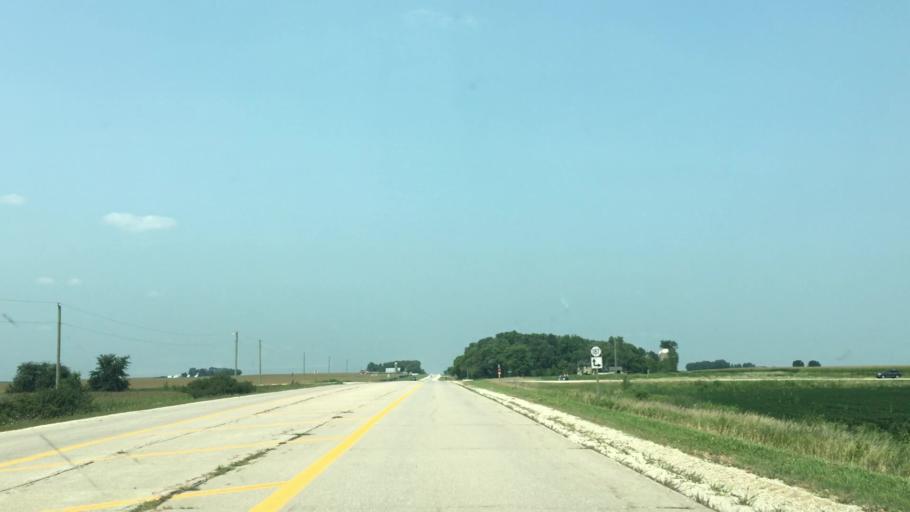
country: US
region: Iowa
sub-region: Fayette County
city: Fayette
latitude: 42.7584
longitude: -91.8043
